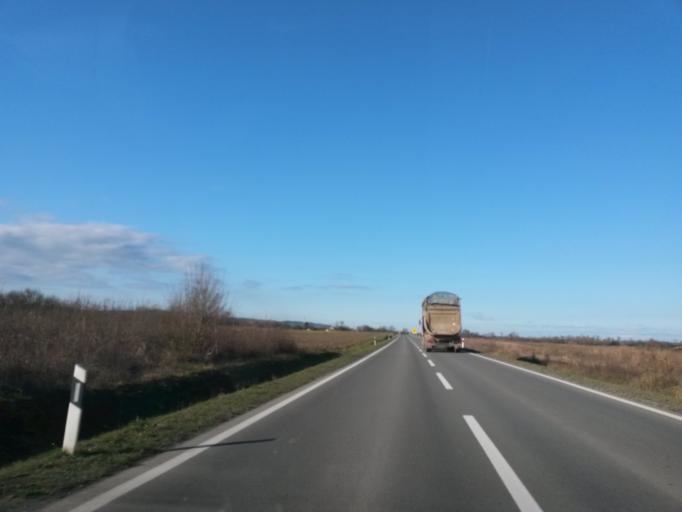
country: HR
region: Virovitick-Podravska
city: Slatina
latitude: 45.7264
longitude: 17.6671
